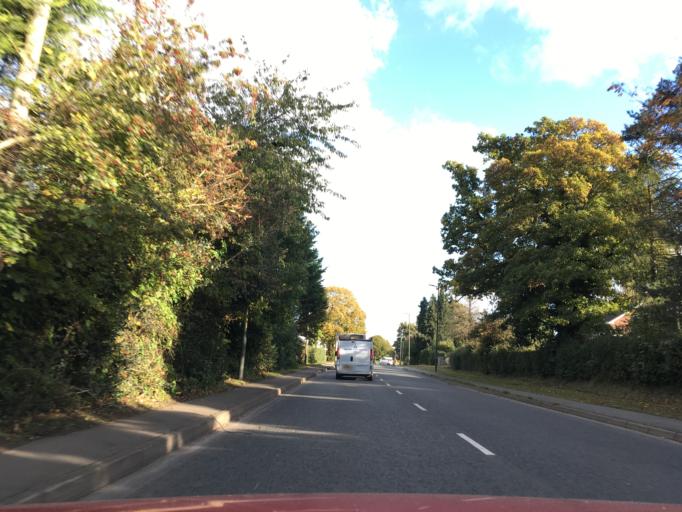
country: GB
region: England
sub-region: Herefordshire
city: Belmont
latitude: 52.0642
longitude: -2.7478
